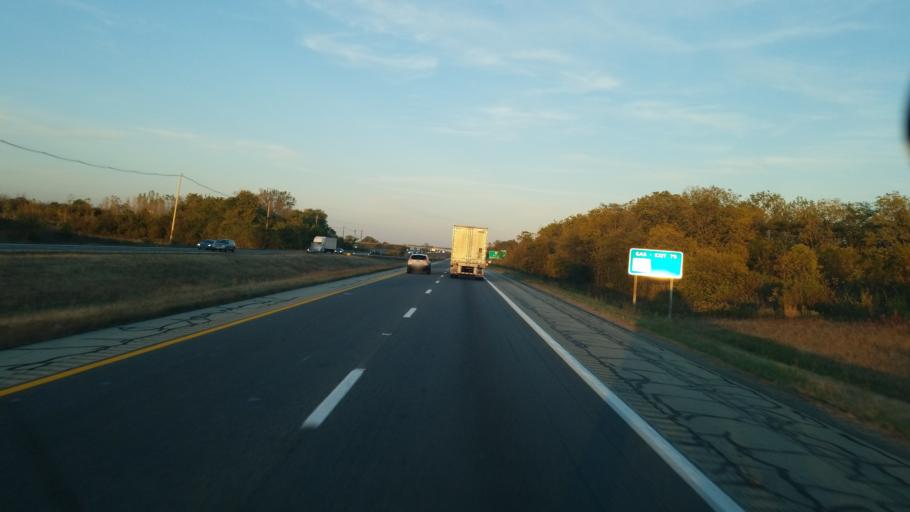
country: US
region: Ohio
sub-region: Madison County
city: Bethel
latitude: 39.6926
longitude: -83.4644
